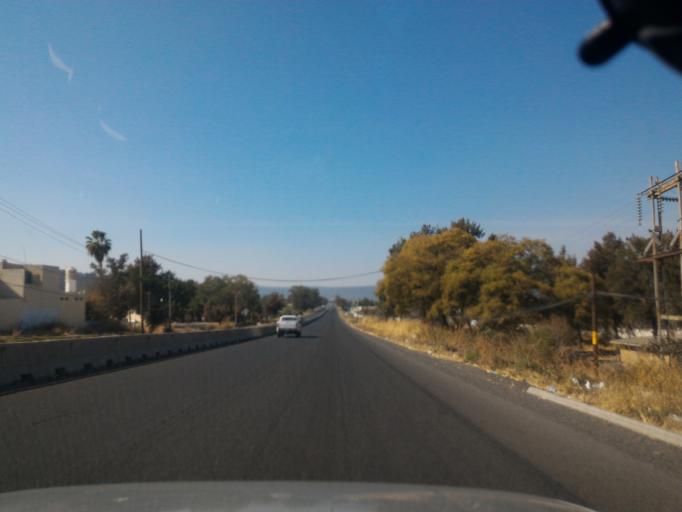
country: MX
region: Jalisco
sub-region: Poncitlan
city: Cuitzeo (La Estancia)
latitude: 20.3501
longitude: -102.7933
